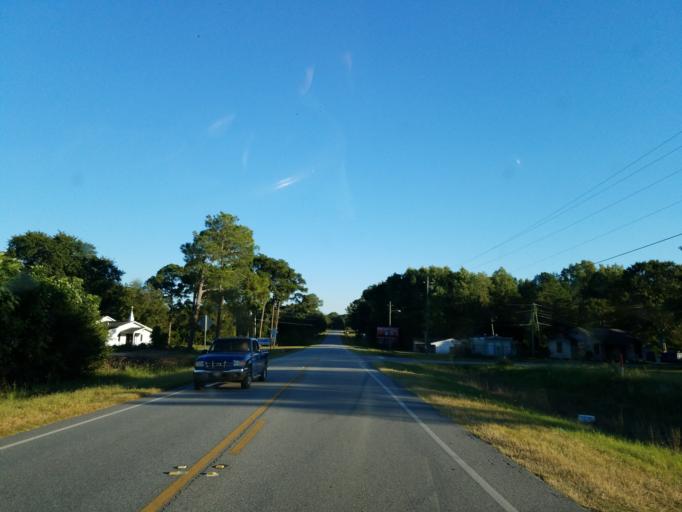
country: US
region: Georgia
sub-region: Worth County
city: Sylvester
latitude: 31.5665
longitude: -83.8534
